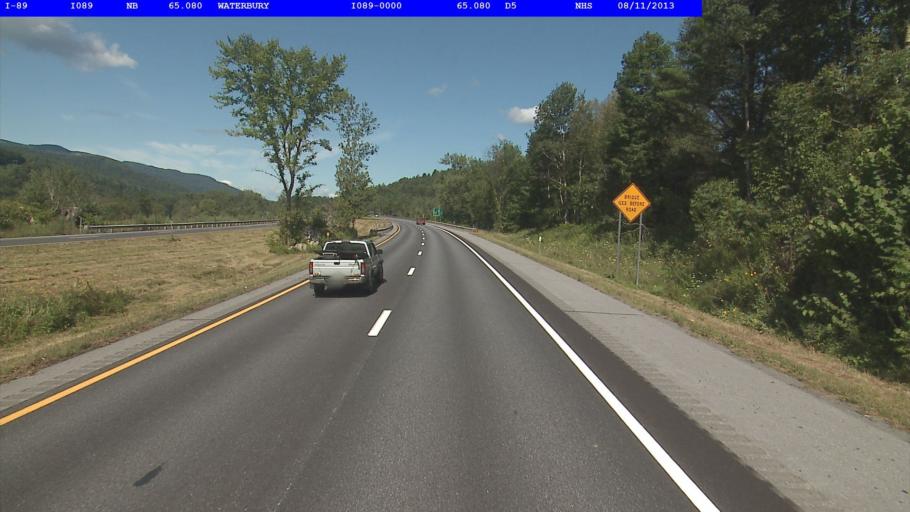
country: US
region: Vermont
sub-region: Washington County
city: Waterbury
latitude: 44.3517
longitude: -72.7749
